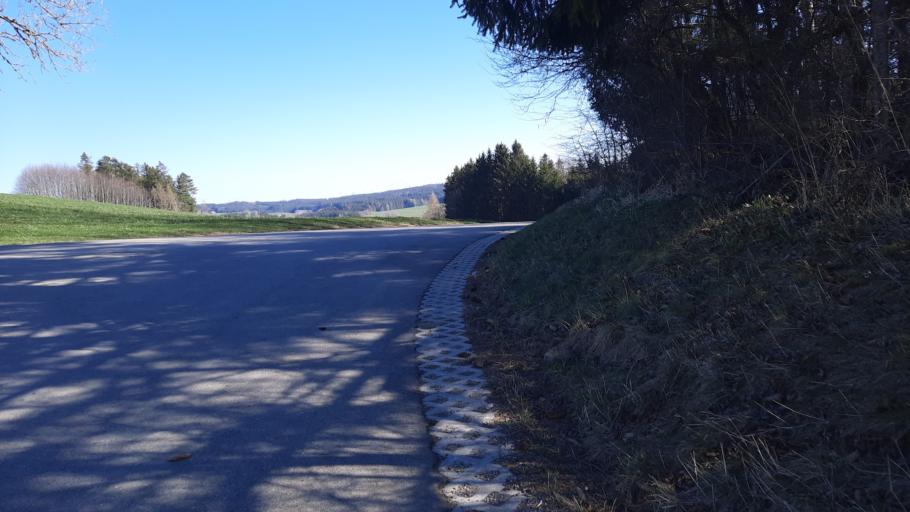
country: DE
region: Bavaria
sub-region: Swabia
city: Haldenwang
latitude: 47.8252
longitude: 10.3377
